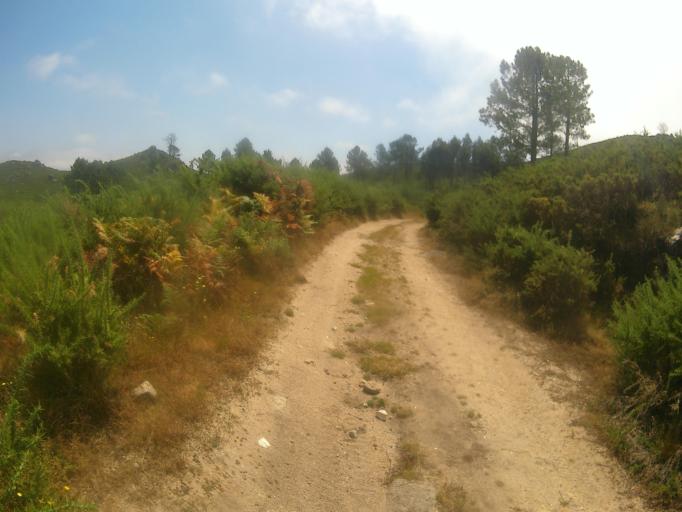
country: PT
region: Viana do Castelo
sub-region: Ponte de Lima
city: Ponte de Lima
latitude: 41.7236
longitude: -8.5984
